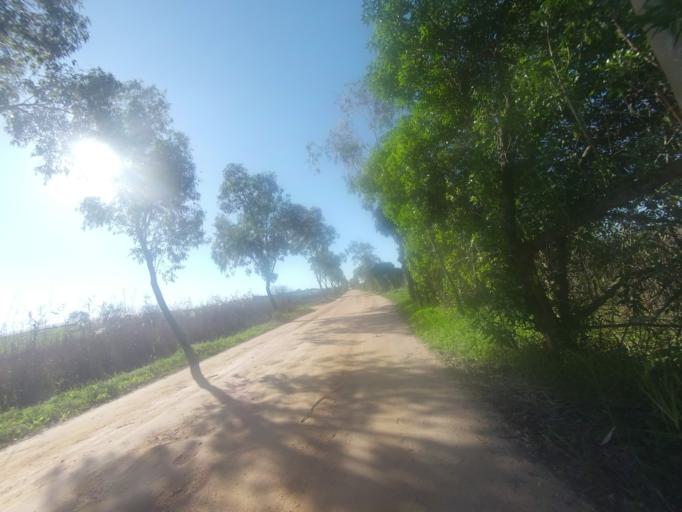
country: ES
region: Andalusia
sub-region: Provincia de Huelva
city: Palos de la Frontera
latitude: 37.2267
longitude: -6.9095
